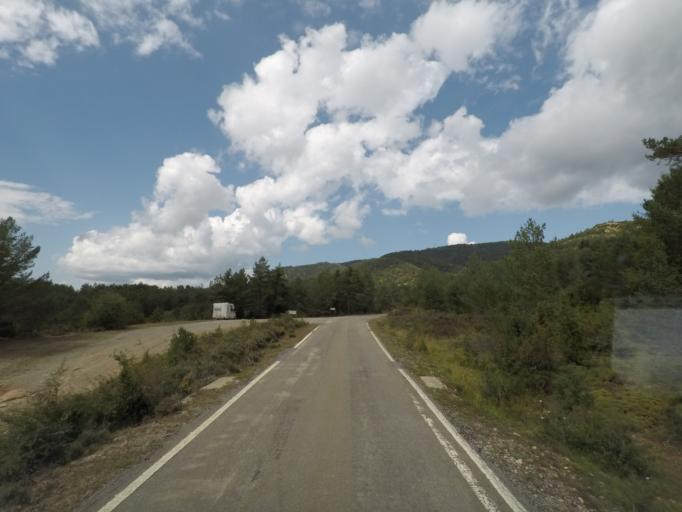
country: ES
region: Aragon
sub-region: Provincia de Huesca
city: Fiscal
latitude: 42.3995
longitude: -0.0459
